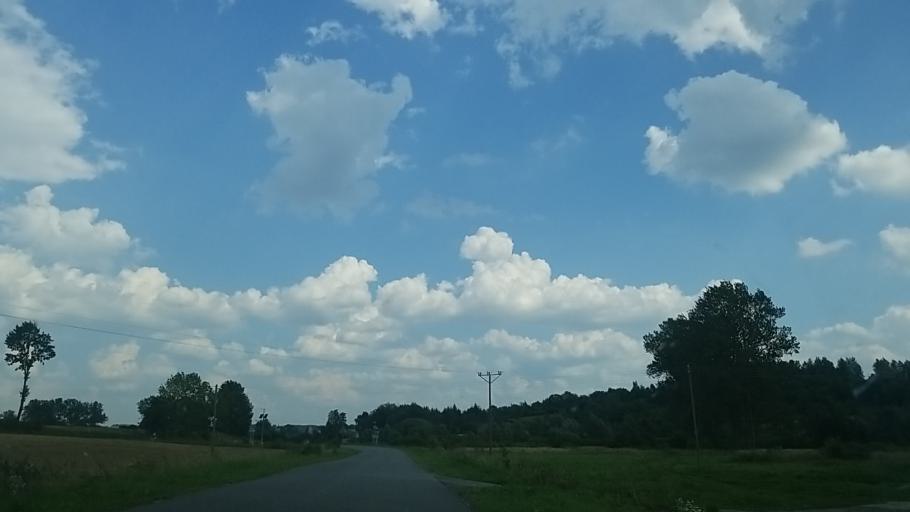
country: PL
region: Lublin Voivodeship
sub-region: Powiat bilgorajski
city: Goraj
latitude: 50.7252
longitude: 22.6513
